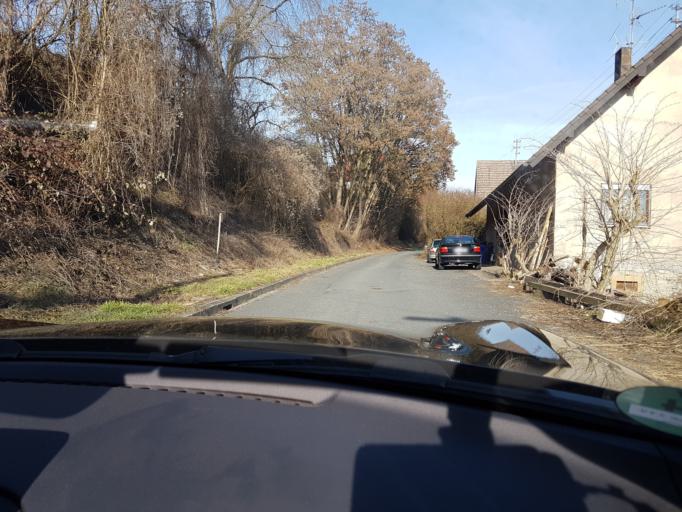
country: DE
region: Baden-Wuerttemberg
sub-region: Karlsruhe Region
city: Osterburken
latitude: 49.4343
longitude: 9.4252
